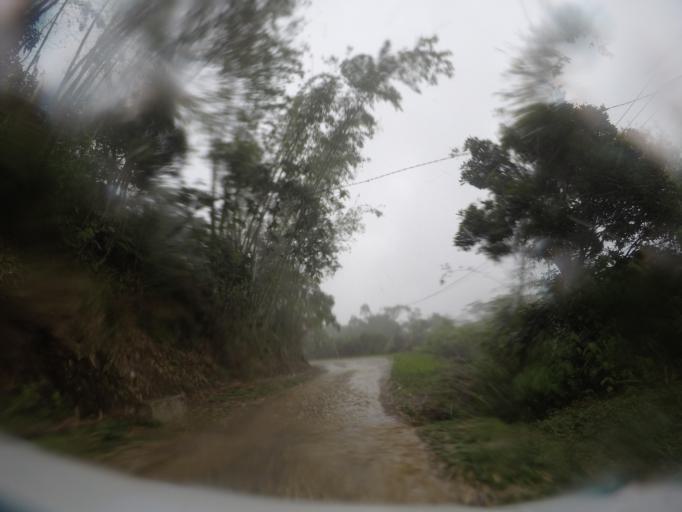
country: TL
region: Baucau
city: Venilale
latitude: -8.6412
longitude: 126.4047
